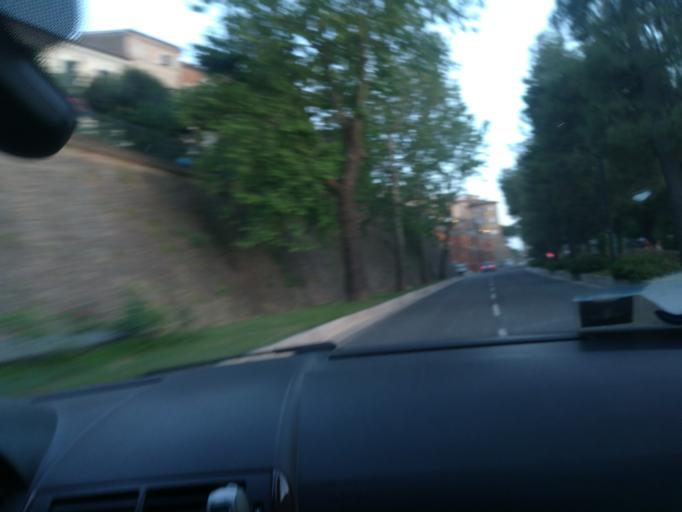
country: IT
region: The Marches
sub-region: Provincia di Macerata
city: Macerata
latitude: 43.2993
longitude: 13.4489
